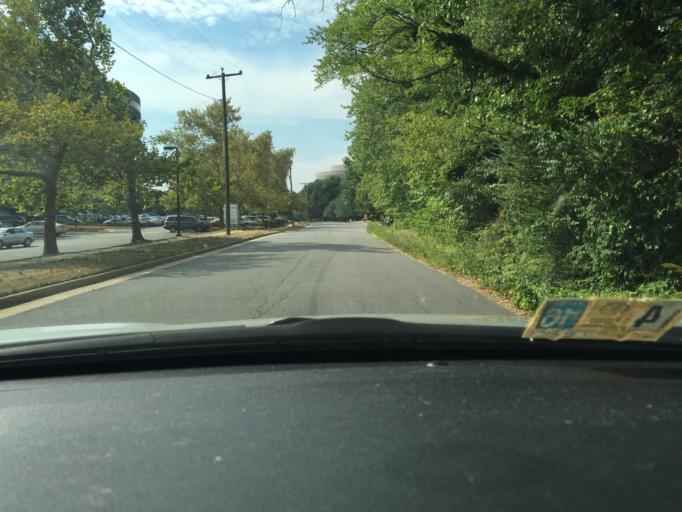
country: US
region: Virginia
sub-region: Fairfax County
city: Tysons Corner
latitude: 38.9152
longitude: -77.2294
